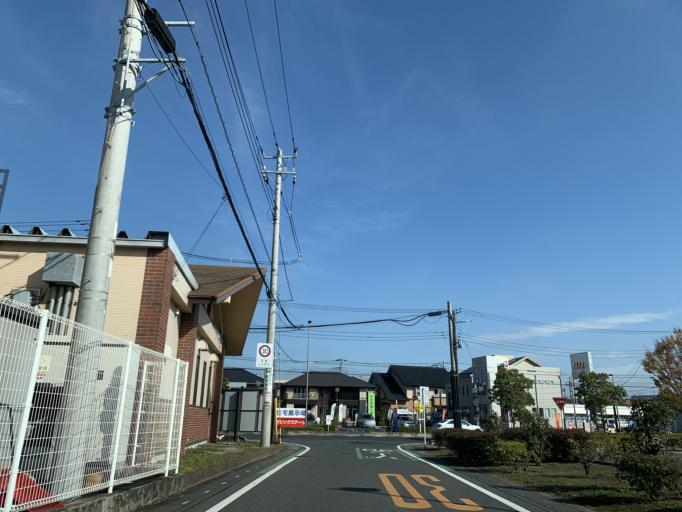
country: JP
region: Saitama
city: Yashio-shi
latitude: 35.8445
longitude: 139.8551
